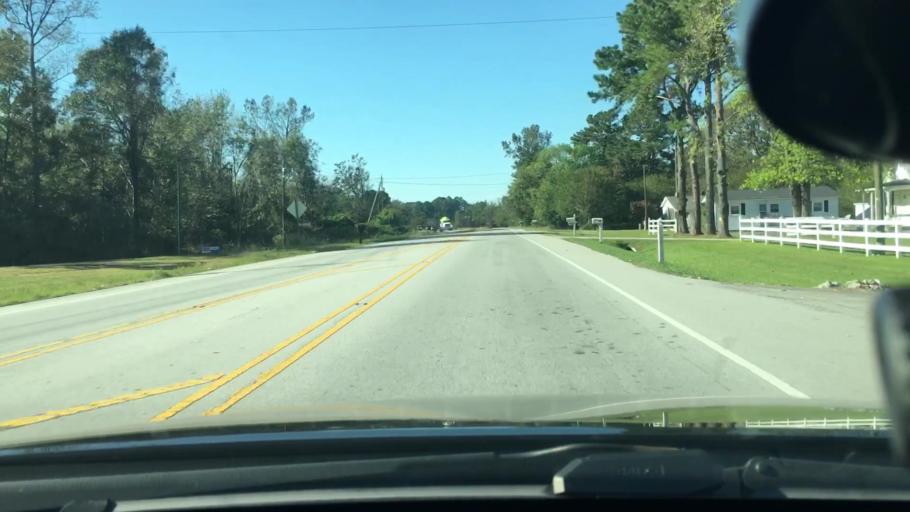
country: US
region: North Carolina
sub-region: Craven County
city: Trent Woods
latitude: 35.1567
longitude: -77.1138
